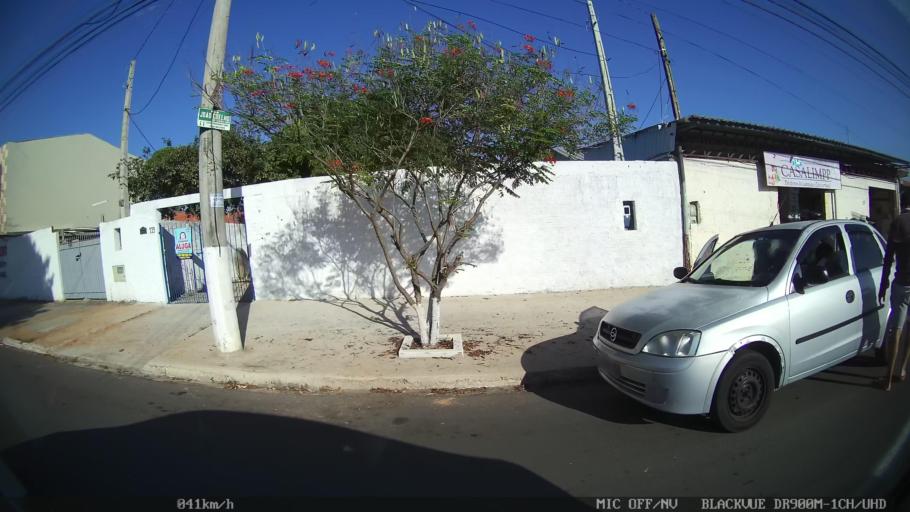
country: BR
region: Sao Paulo
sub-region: Hortolandia
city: Hortolandia
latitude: -22.8955
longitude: -47.1643
